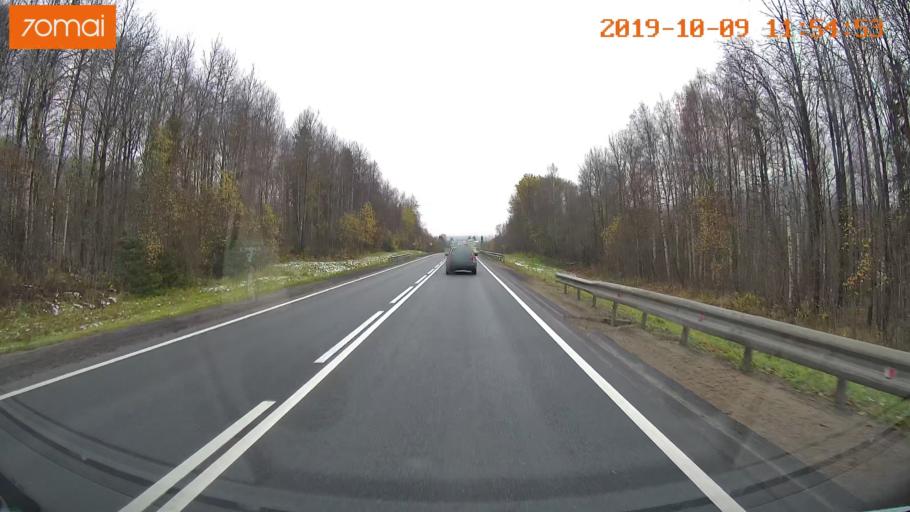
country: RU
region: Vologda
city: Gryazovets
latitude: 58.7538
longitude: 40.2835
